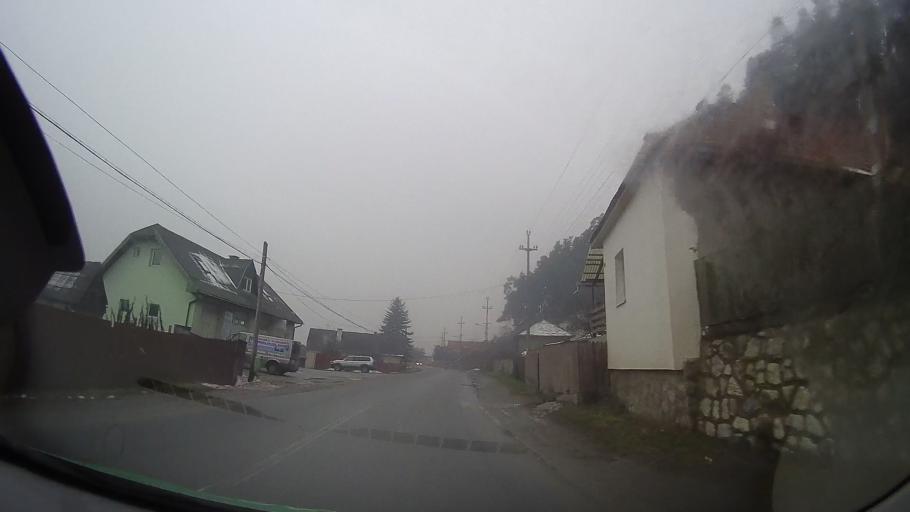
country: RO
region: Harghita
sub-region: Municipiul Gheorgheni
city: Gheorgheni
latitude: 46.7267
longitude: 25.6255
